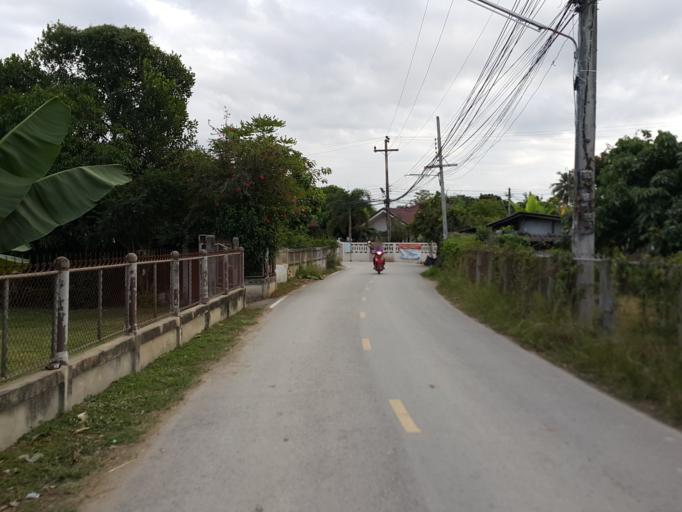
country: TH
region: Chiang Mai
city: San Sai
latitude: 18.8682
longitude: 99.1126
